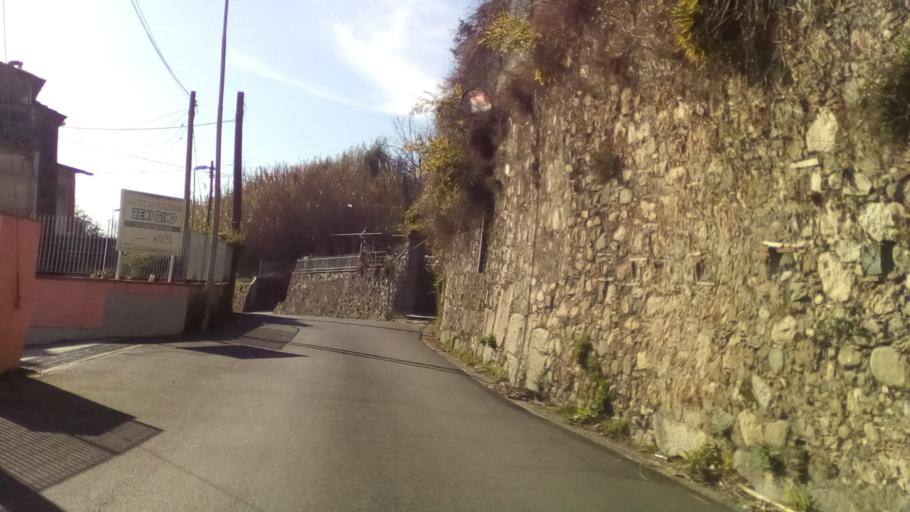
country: IT
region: Tuscany
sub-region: Provincia di Massa-Carrara
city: Carrara
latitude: 44.0721
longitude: 10.0851
